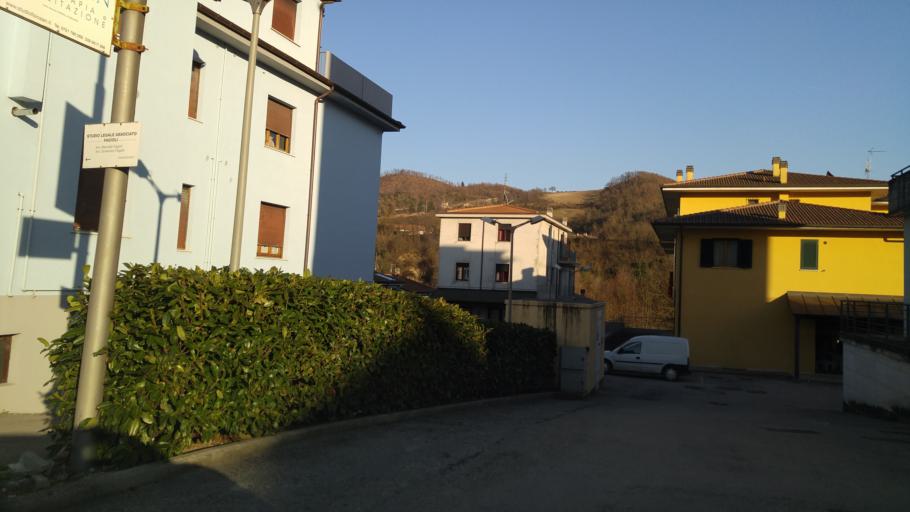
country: IT
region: The Marches
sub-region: Provincia di Pesaro e Urbino
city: Cagli
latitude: 43.5528
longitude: 12.6523
